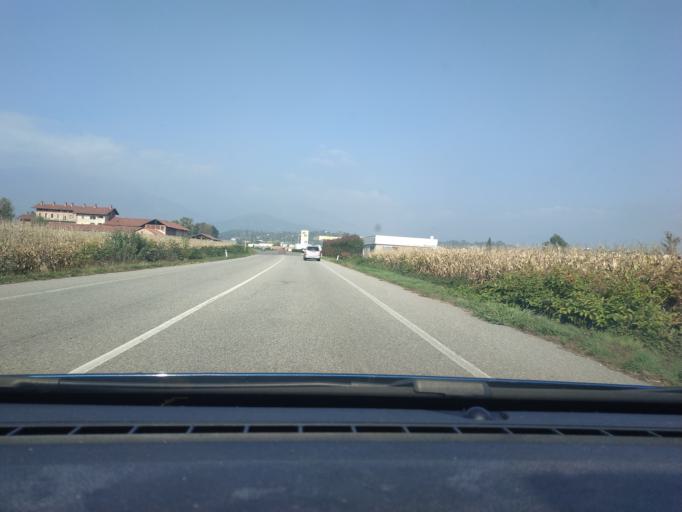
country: IT
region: Piedmont
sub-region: Provincia di Biella
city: Occhieppo Inferiore
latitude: 45.5444
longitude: 8.0369
